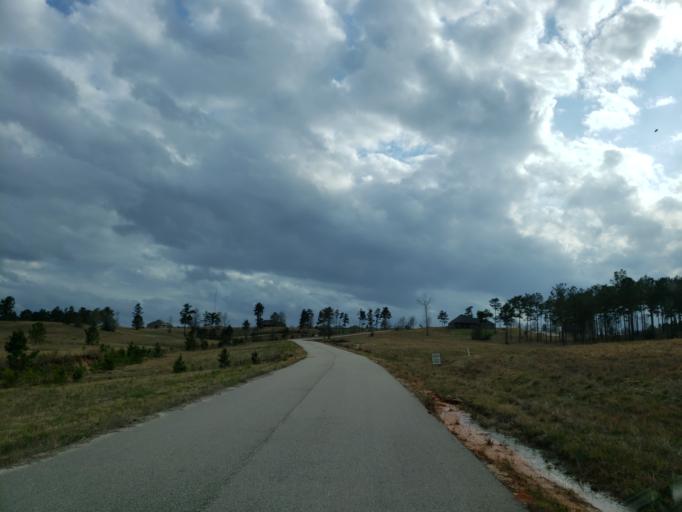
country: US
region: Mississippi
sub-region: Jones County
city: Ellisville
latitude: 31.5630
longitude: -89.2534
